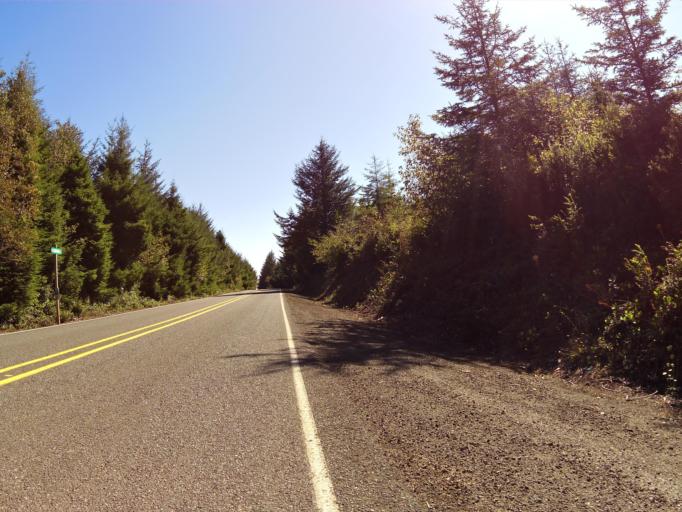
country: US
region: Oregon
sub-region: Coos County
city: Barview
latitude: 43.2648
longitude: -124.3442
